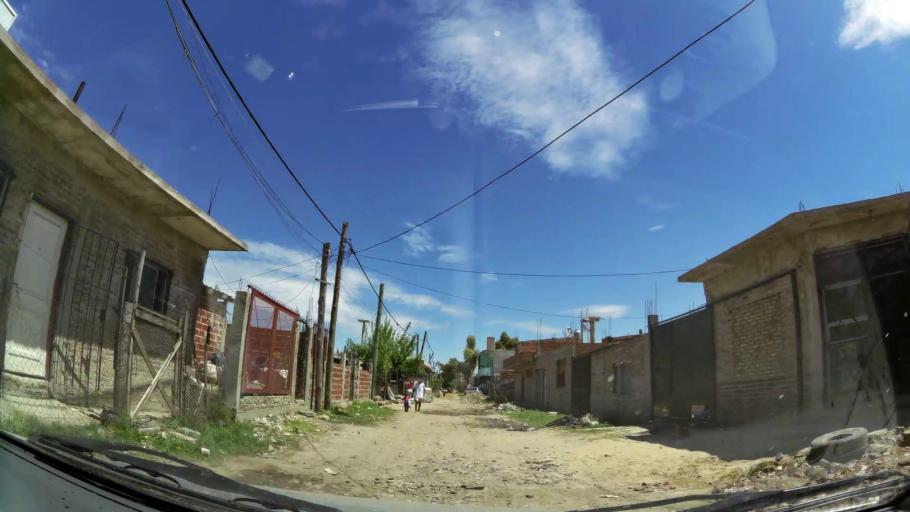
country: AR
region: Buenos Aires
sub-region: Partido de Quilmes
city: Quilmes
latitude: -34.7298
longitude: -58.3167
